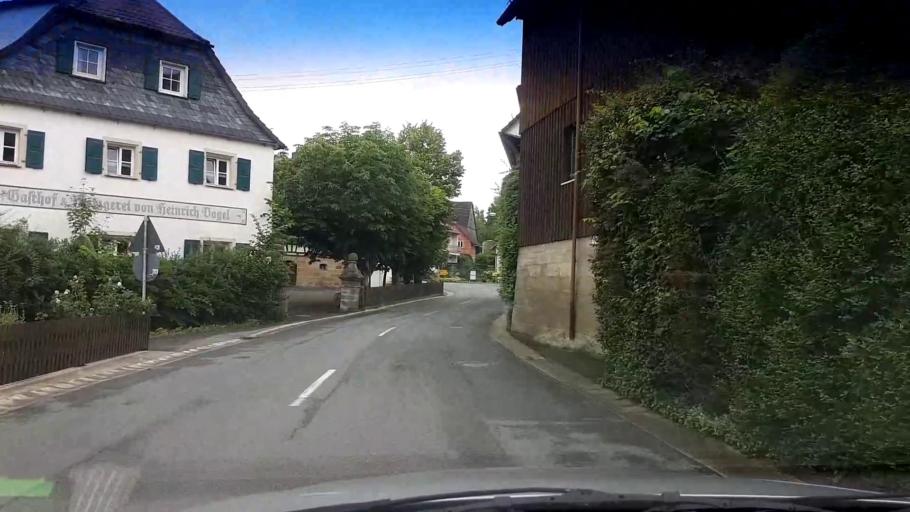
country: DE
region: Bavaria
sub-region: Upper Franconia
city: Kasendorf
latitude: 50.0775
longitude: 11.3179
